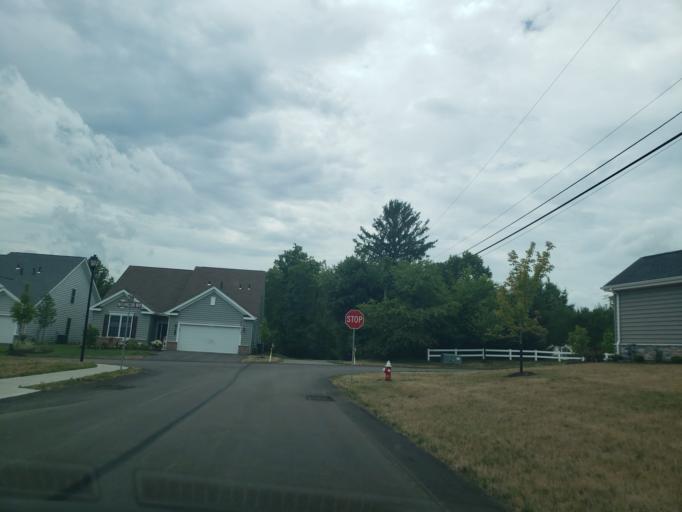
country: US
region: Pennsylvania
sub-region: Allegheny County
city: Emsworth
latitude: 40.5351
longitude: -80.0915
